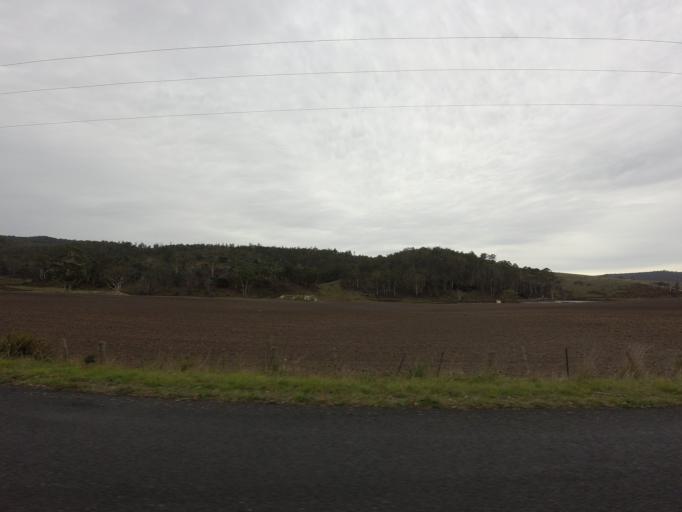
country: AU
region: Tasmania
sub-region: Derwent Valley
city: New Norfolk
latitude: -42.5989
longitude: 147.0520
